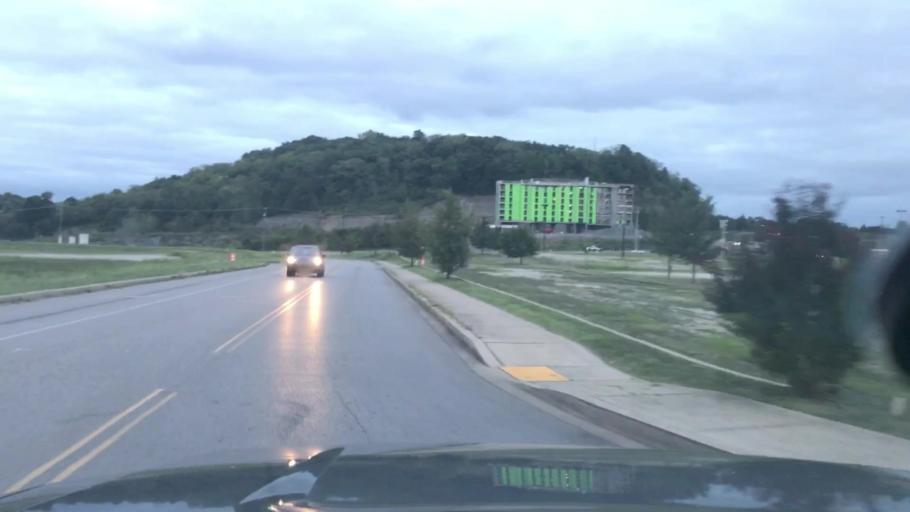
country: US
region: Tennessee
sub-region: Davidson County
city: Nashville
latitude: 36.2455
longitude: -86.7601
